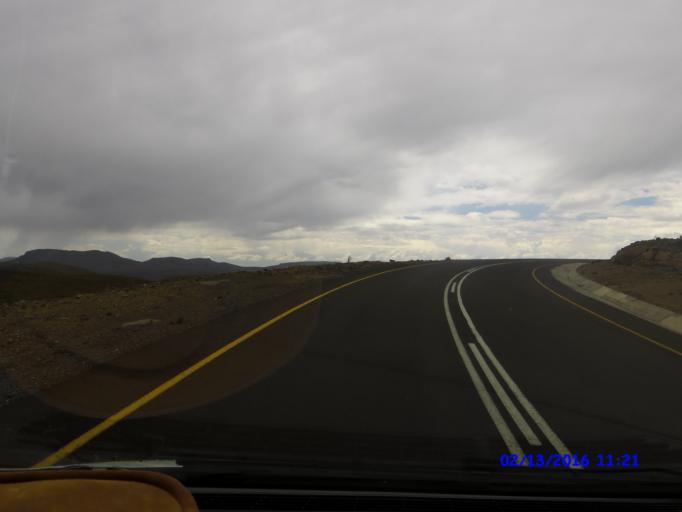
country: LS
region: Maseru
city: Nako
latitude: -29.7535
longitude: 27.9765
